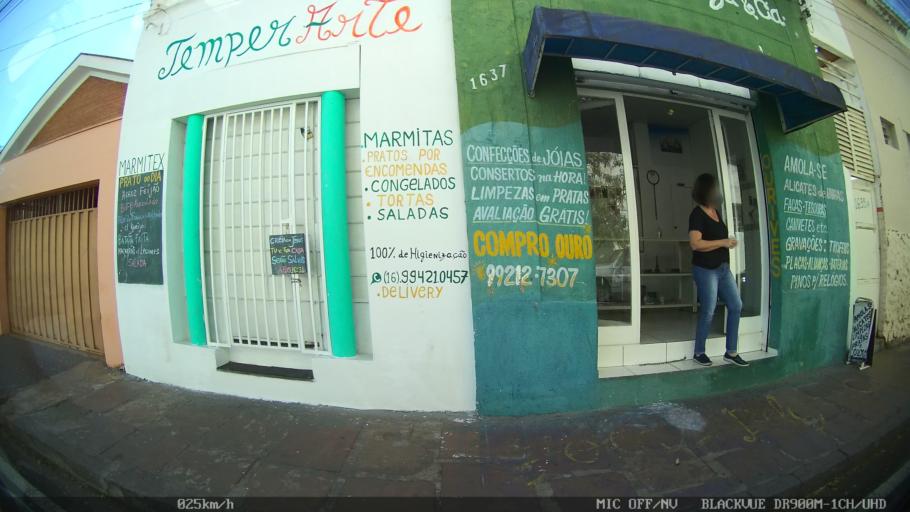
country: BR
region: Sao Paulo
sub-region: Franca
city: Franca
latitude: -20.5353
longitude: -47.3987
